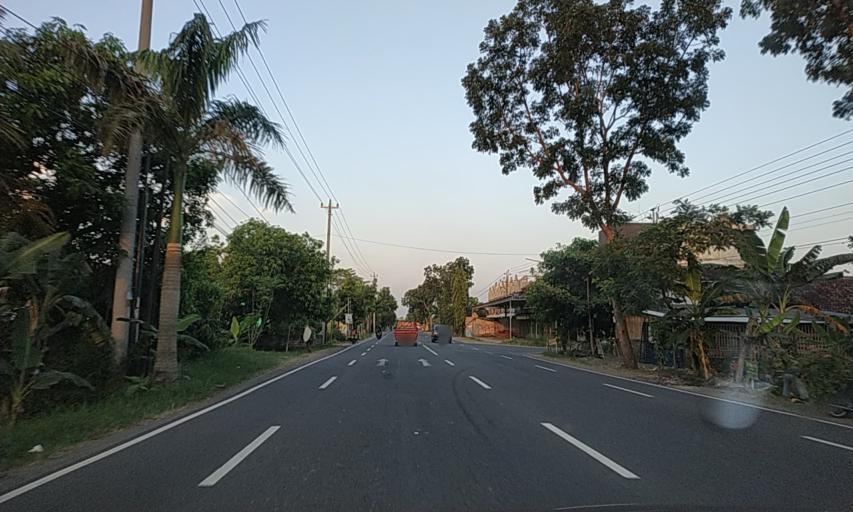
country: ID
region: Daerah Istimewa Yogyakarta
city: Srandakan
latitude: -7.8907
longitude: 110.1169
